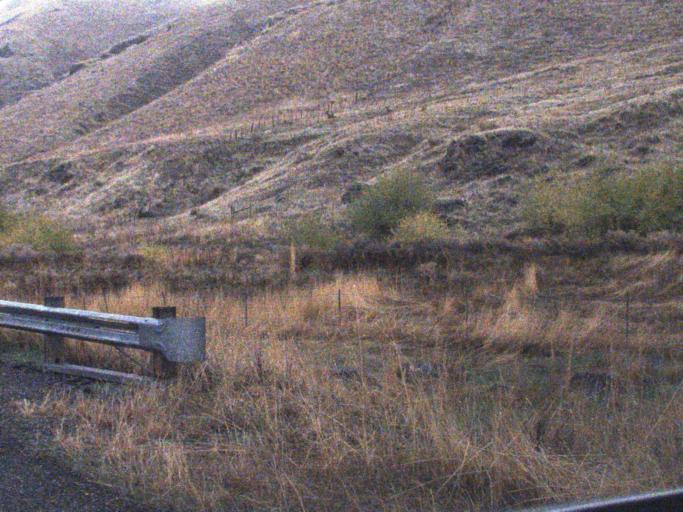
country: US
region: Washington
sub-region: Asotin County
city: Clarkston Heights-Vineland
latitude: 46.4299
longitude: -117.1214
